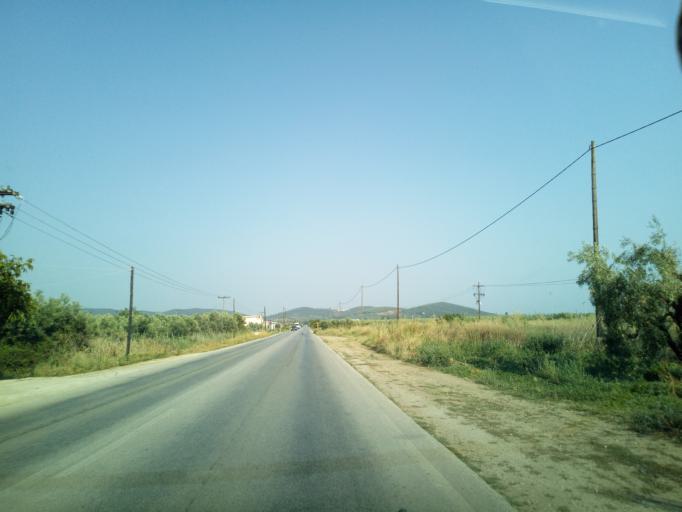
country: GR
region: Central Macedonia
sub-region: Nomos Chalkidikis
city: Ormylia
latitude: 40.2612
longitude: 23.5223
